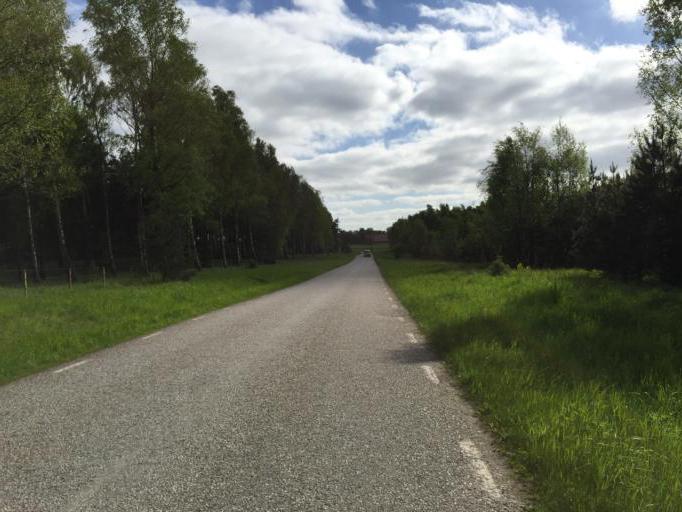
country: SE
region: Skane
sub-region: Sjobo Kommun
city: Blentarp
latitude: 55.6548
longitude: 13.6070
